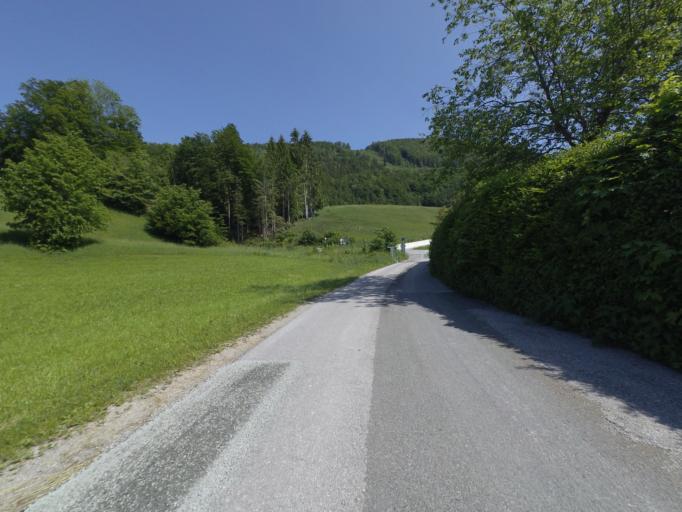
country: AT
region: Salzburg
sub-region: Politischer Bezirk Salzburg-Umgebung
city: Koppl
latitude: 47.7754
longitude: 13.1368
